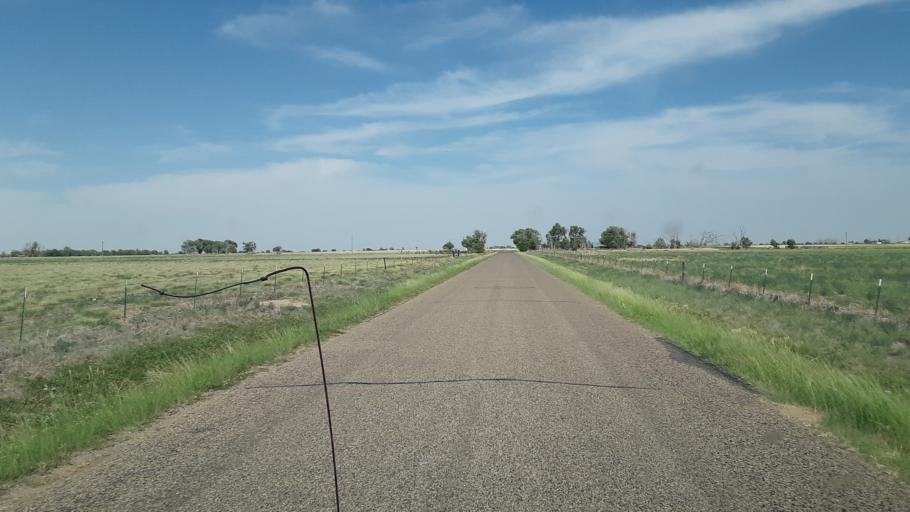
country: US
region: Colorado
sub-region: Crowley County
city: Ordway
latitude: 38.1632
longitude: -103.8618
